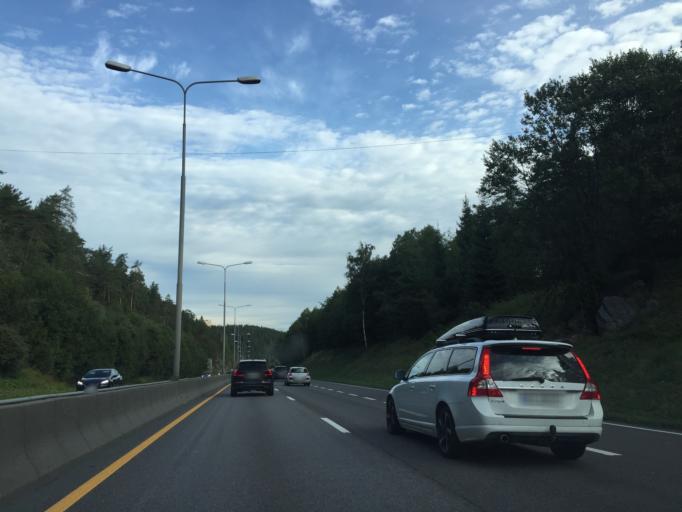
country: NO
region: Akershus
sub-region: Oppegard
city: Kolbotn
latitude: 59.8525
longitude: 10.8341
